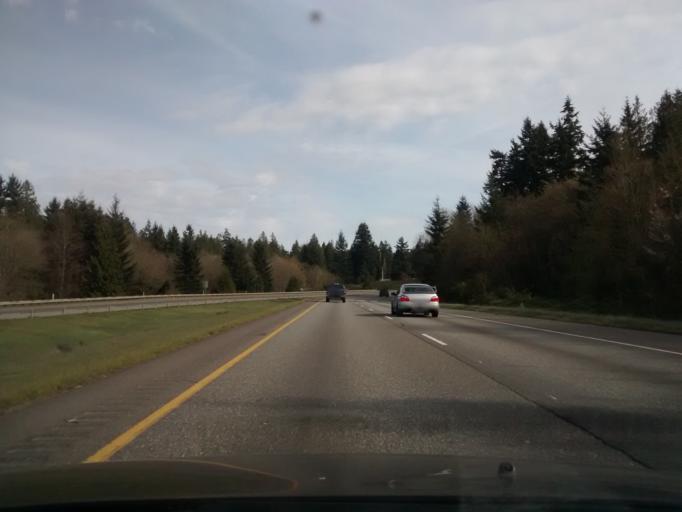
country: US
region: Washington
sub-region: Kitsap County
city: Silverdale
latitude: 47.6553
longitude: -122.7052
